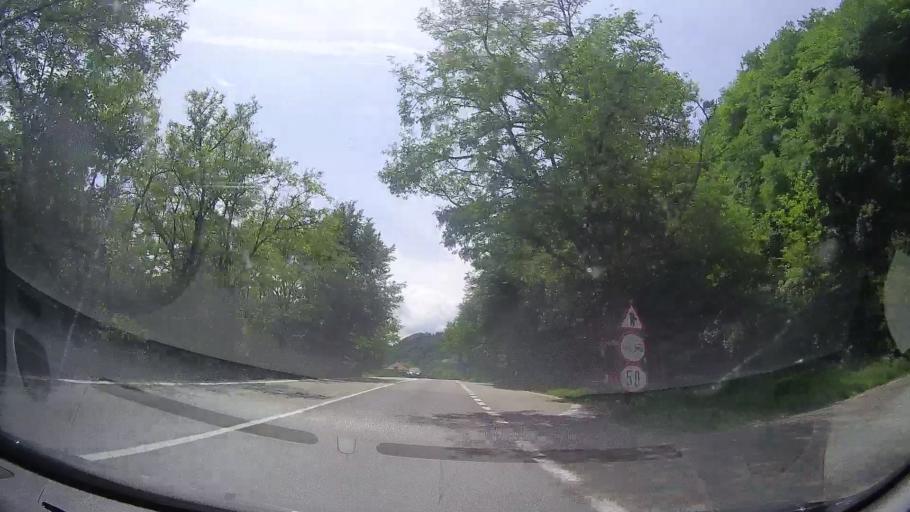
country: RO
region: Valcea
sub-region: Comuna Racovita
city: Racovita
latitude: 45.3888
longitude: 24.3024
